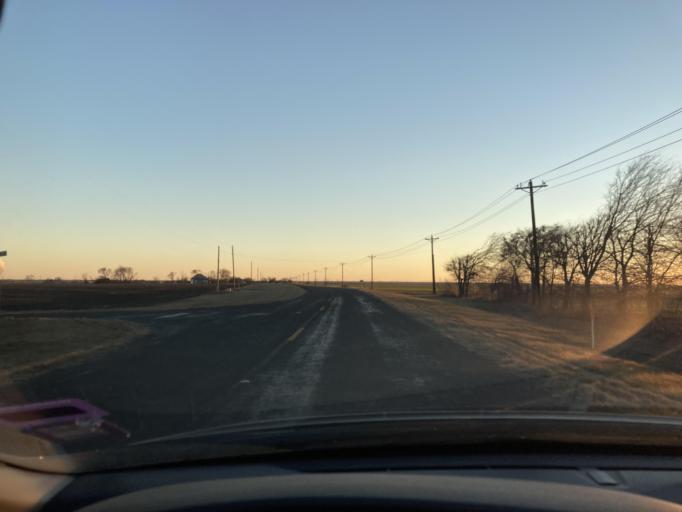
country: US
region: Texas
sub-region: Ellis County
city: Nash
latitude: 32.2882
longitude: -96.8969
